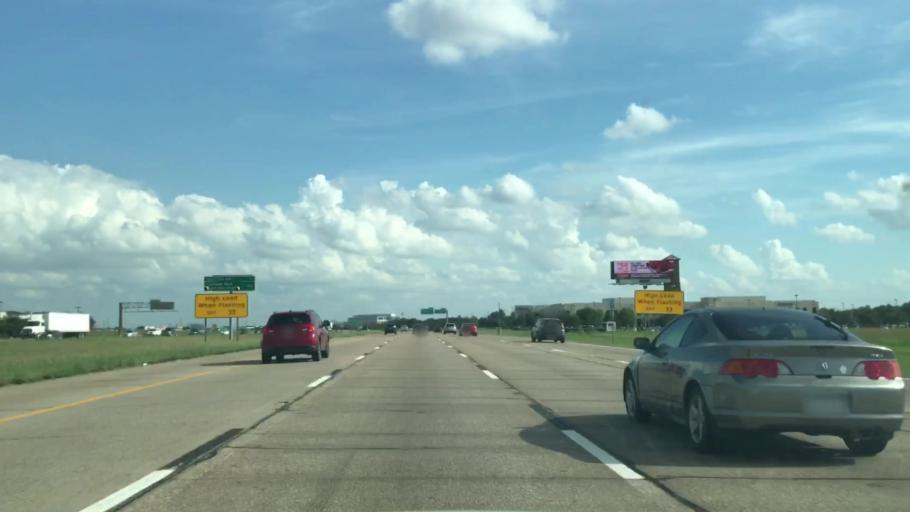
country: US
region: Texas
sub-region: Dallas County
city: Coppell
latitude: 32.9314
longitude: -97.0056
